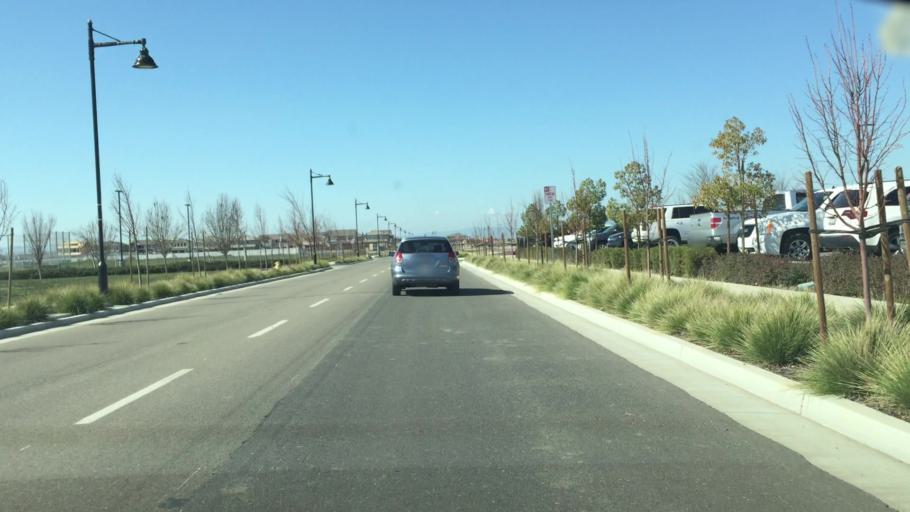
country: US
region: California
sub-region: San Joaquin County
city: Lathrop
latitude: 37.7988
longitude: -121.3190
